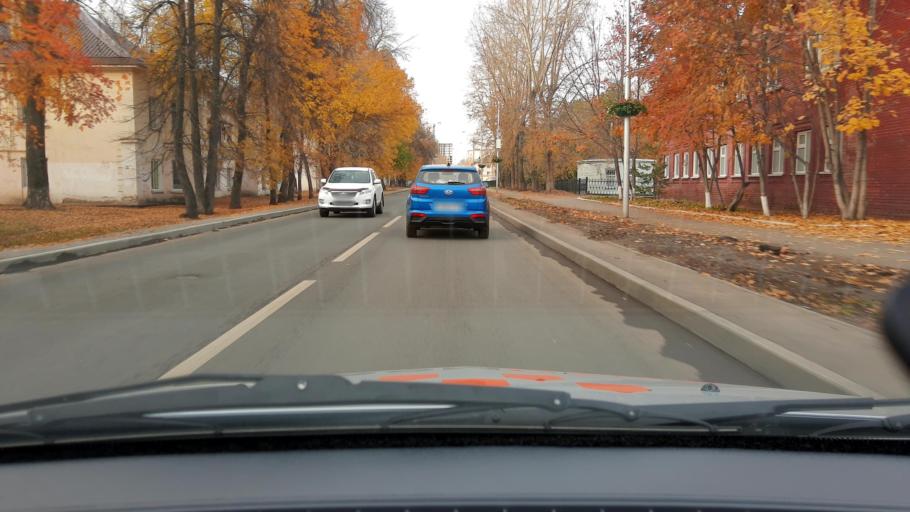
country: RU
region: Bashkortostan
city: Mikhaylovka
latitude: 54.7020
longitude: 55.8360
